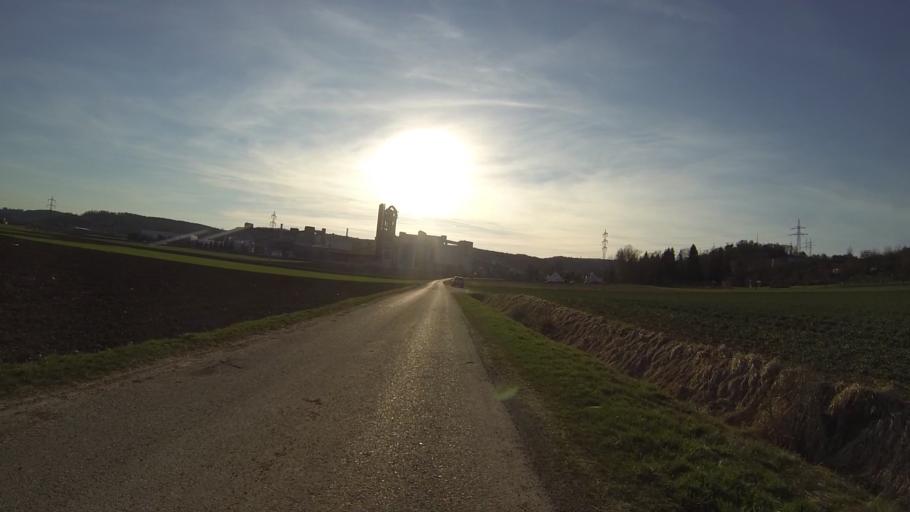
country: DE
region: Baden-Wuerttemberg
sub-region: Regierungsbezirk Stuttgart
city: Bolheim
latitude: 48.6538
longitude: 10.1708
